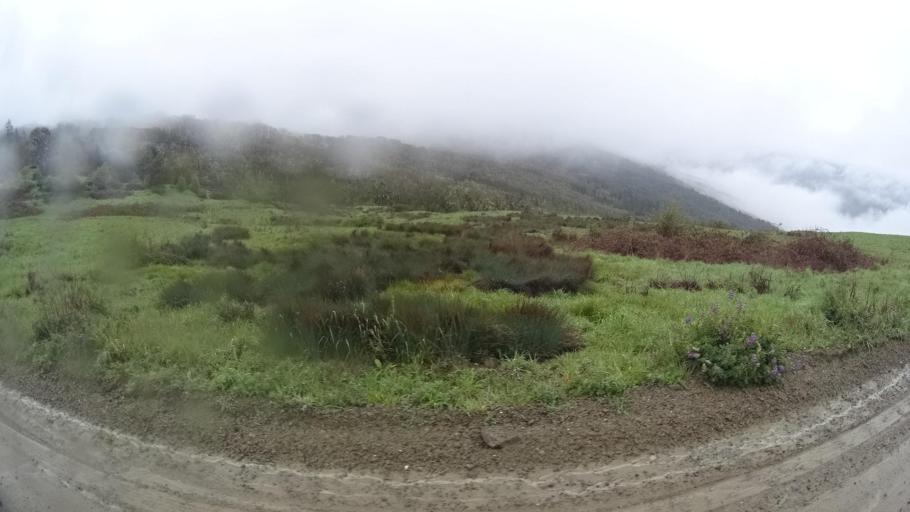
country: US
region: California
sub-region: Humboldt County
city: Westhaven-Moonstone
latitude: 41.1570
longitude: -123.8908
